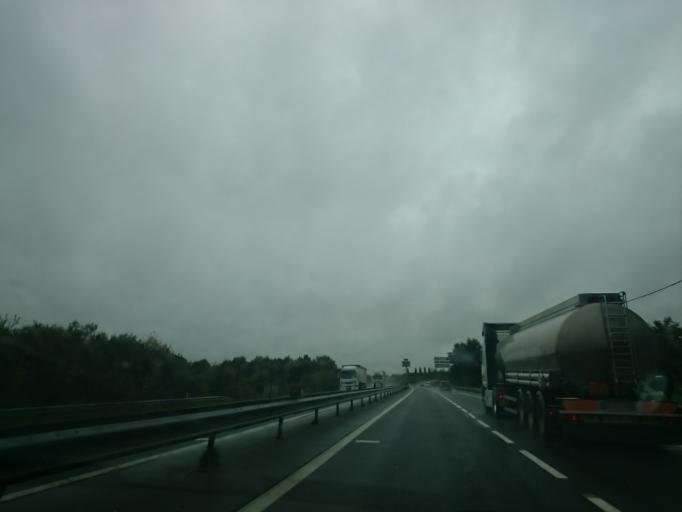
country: FR
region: Pays de la Loire
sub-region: Departement de la Loire-Atlantique
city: Pontchateau
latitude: 47.4268
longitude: -2.0594
